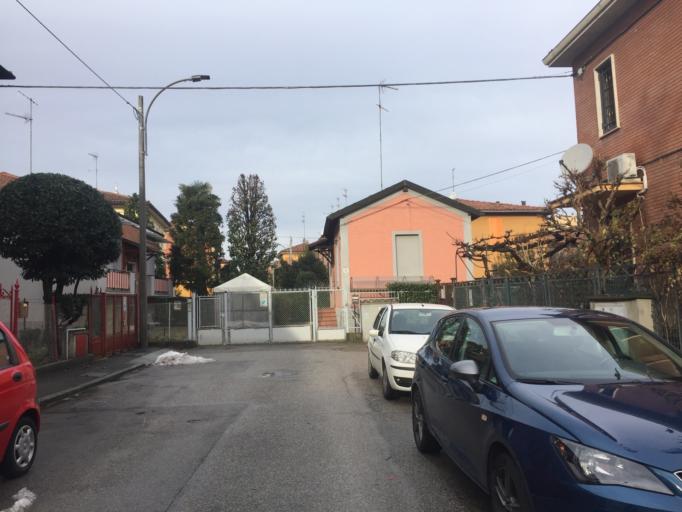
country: IT
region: Emilia-Romagna
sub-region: Provincia di Bologna
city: Casalecchio di Reno
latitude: 44.5058
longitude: 11.3000
